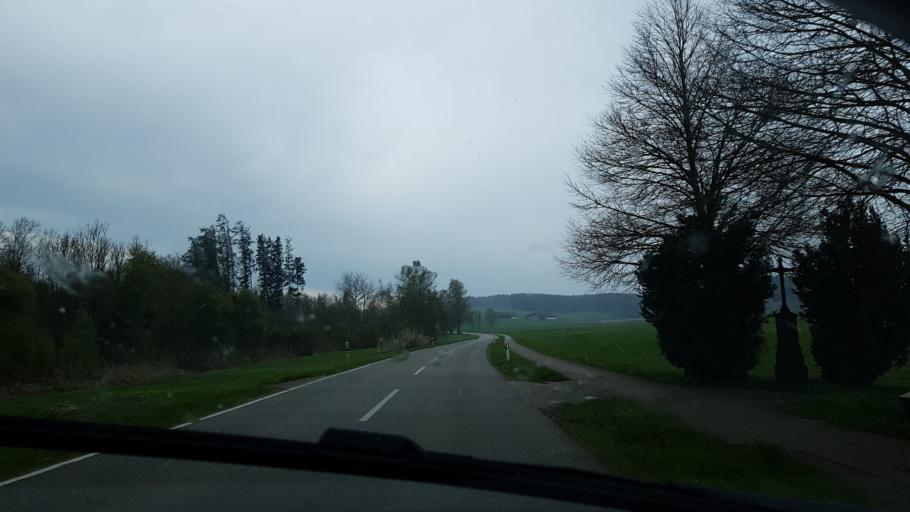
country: DE
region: Baden-Wuerttemberg
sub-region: Tuebingen Region
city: Wain
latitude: 48.2258
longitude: 10.0190
